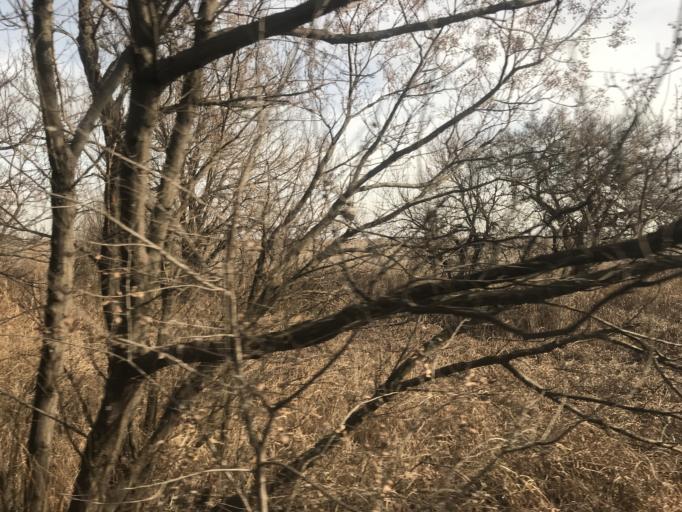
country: AR
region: Cordoba
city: Laguna Larga
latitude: -31.7356
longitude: -63.8391
